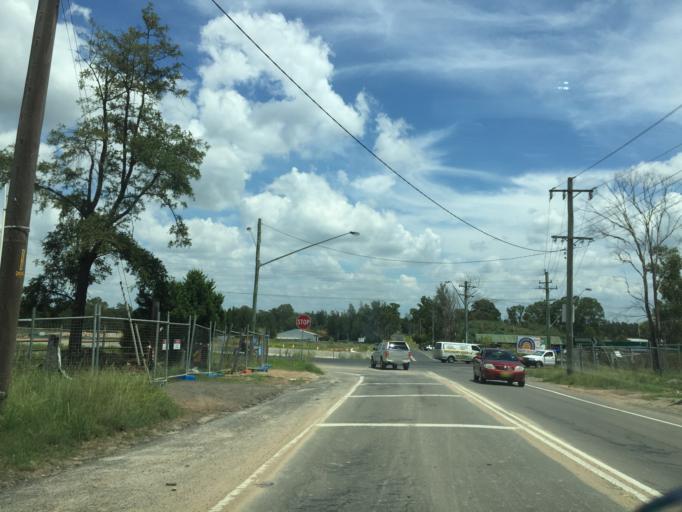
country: AU
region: New South Wales
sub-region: Blacktown
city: Hassall Grove
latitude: -33.7036
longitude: 150.8376
